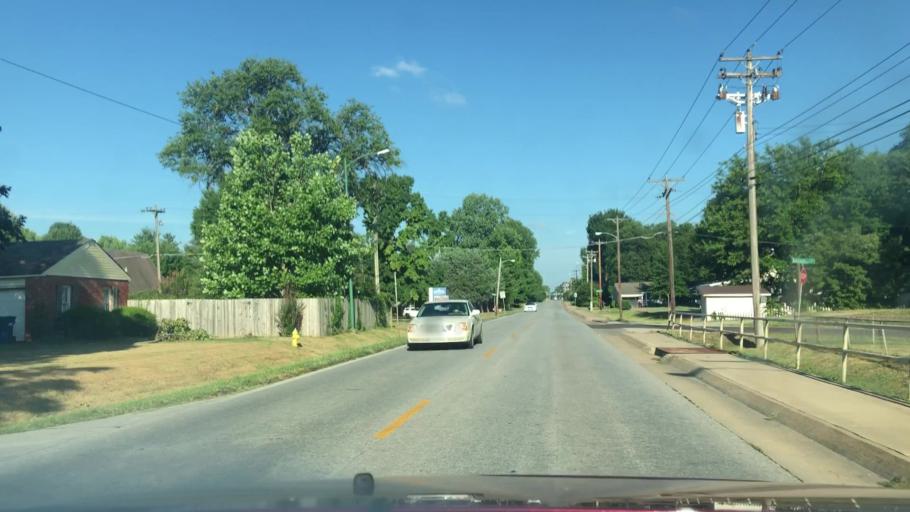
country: US
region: Missouri
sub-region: Greene County
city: Springfield
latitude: 37.1739
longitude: -93.2529
